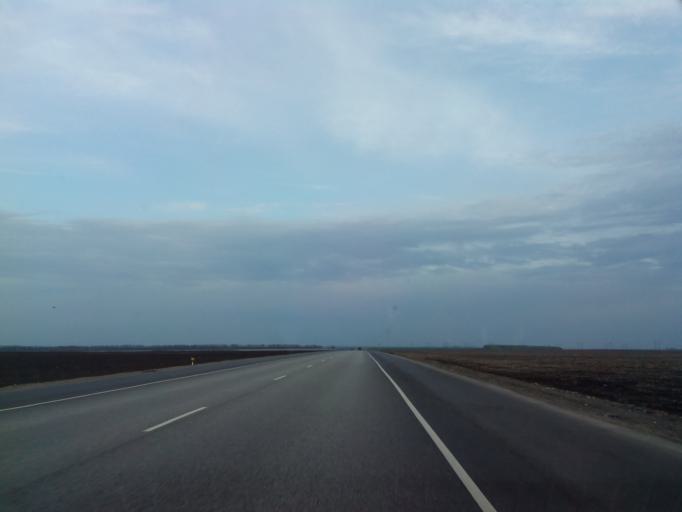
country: RU
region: Rjazan
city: Ryazhsk
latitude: 53.5719
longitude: 40.0464
